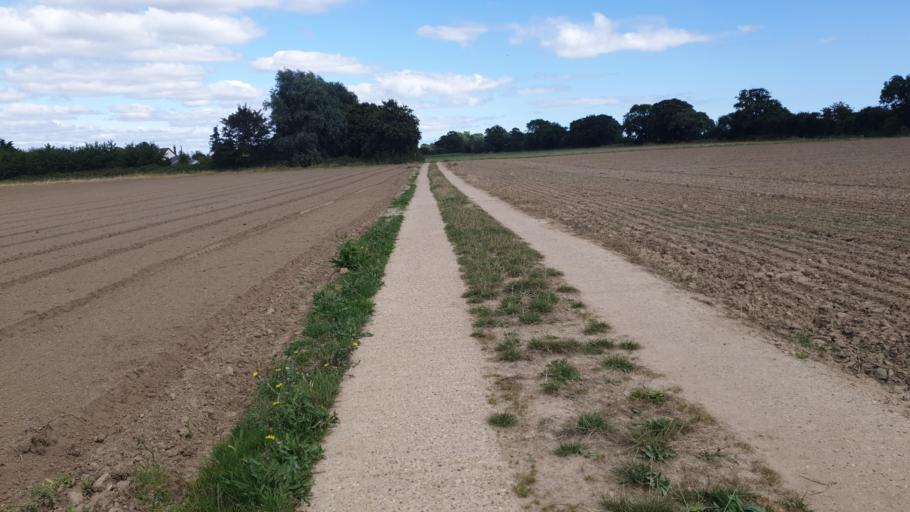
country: GB
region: England
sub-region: Essex
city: Dovercourt
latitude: 51.9046
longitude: 1.1968
